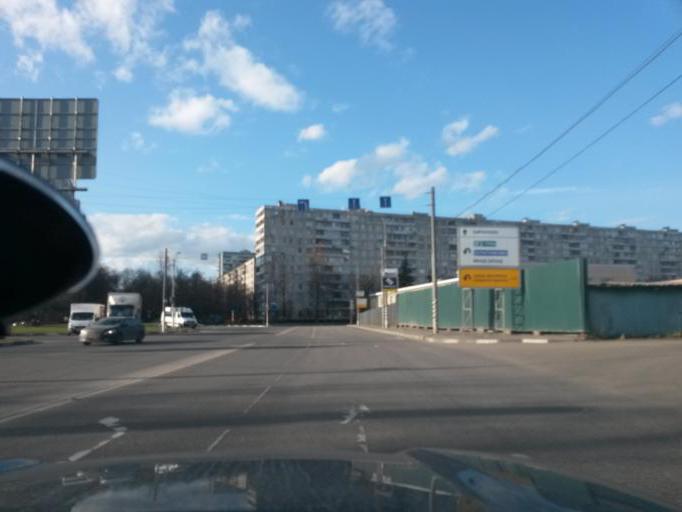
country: RU
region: Moscow
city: Zagor'ye
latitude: 55.5740
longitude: 37.6532
